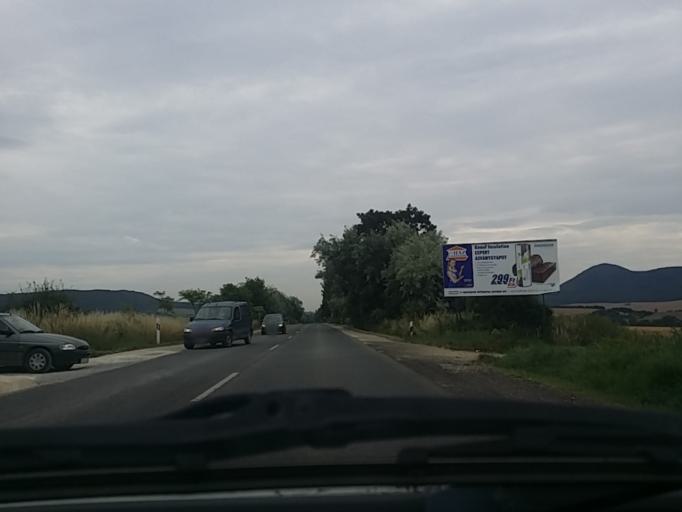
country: HU
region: Pest
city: Solymar
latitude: 47.6041
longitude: 18.9515
